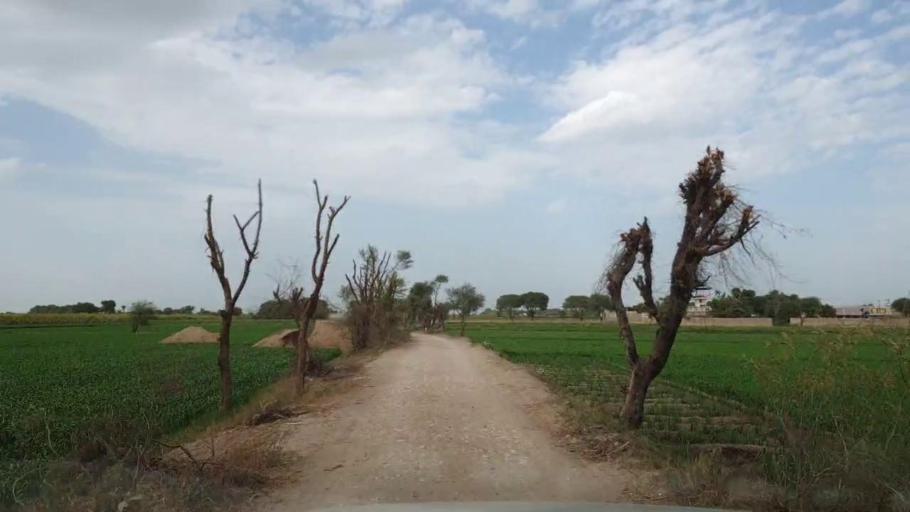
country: PK
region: Sindh
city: Tando Jam
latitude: 25.5461
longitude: 68.5861
